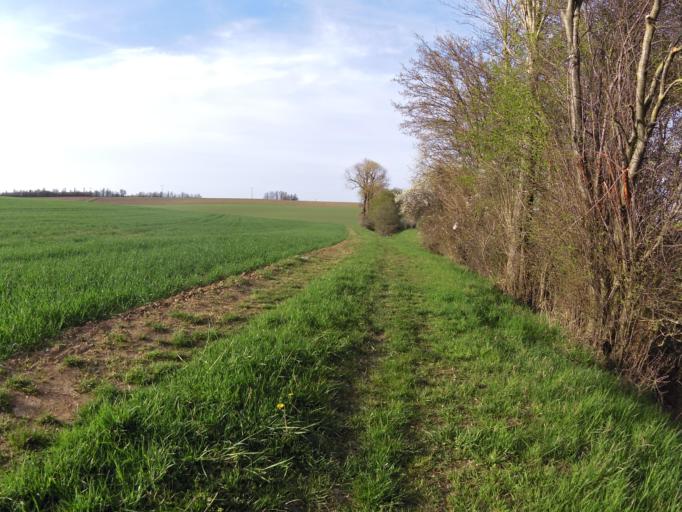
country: DE
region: Bavaria
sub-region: Regierungsbezirk Unterfranken
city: Biebelried
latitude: 49.7852
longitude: 10.1112
